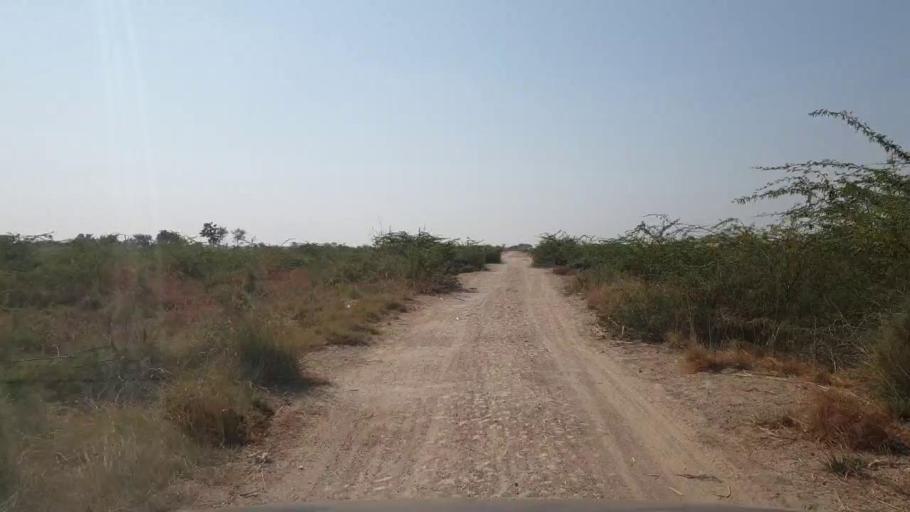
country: PK
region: Sindh
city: Samaro
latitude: 25.2460
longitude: 69.2880
